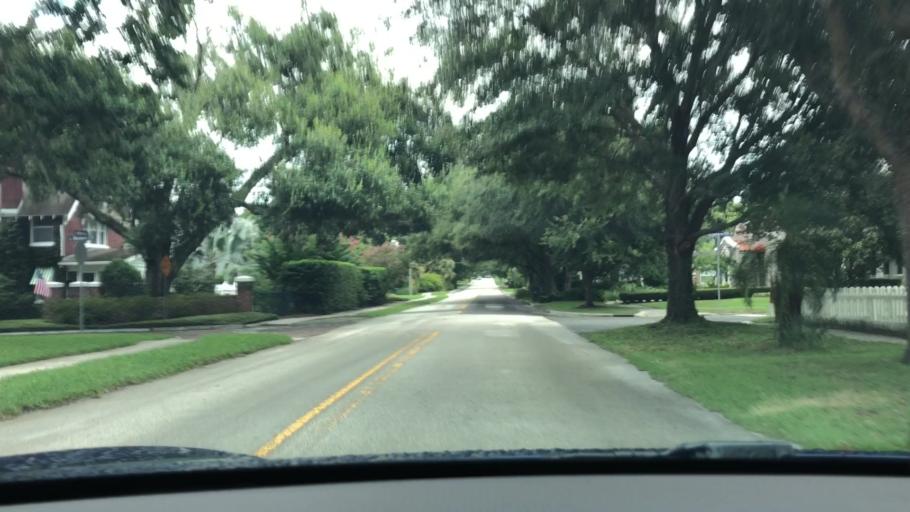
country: US
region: Florida
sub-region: Orange County
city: Winter Park
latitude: 28.5706
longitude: -81.3461
